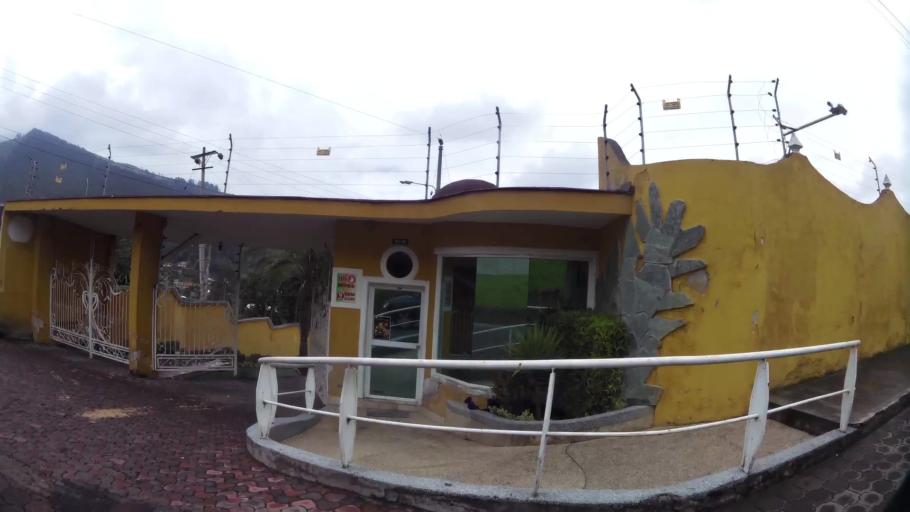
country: EC
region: Pichincha
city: Sangolqui
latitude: -0.2915
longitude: -78.4411
